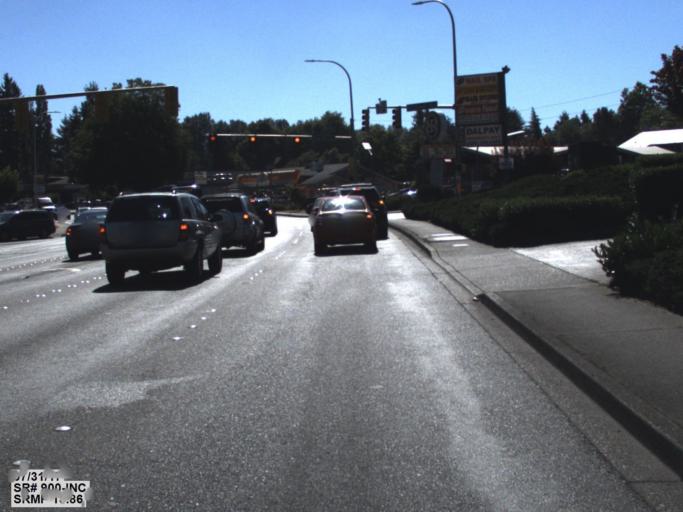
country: US
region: Washington
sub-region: King County
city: Newcastle
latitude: 47.5042
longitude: -122.1654
